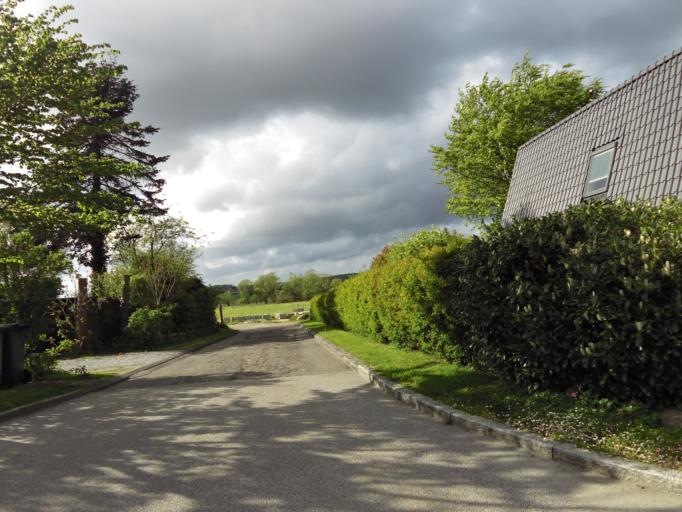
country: DK
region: South Denmark
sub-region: Haderslev Kommune
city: Gram
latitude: 55.2951
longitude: 9.0461
